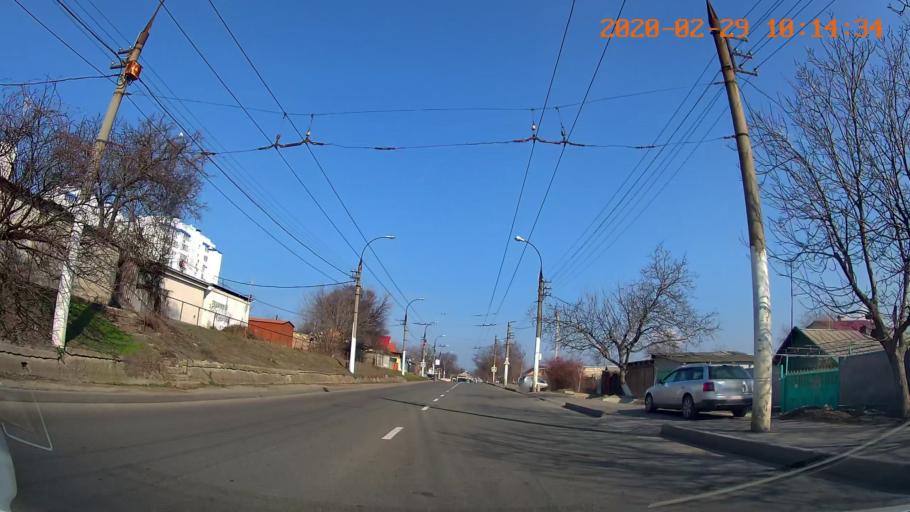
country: MD
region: Telenesti
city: Tiraspolul Nou
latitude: 46.8480
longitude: 29.6434
